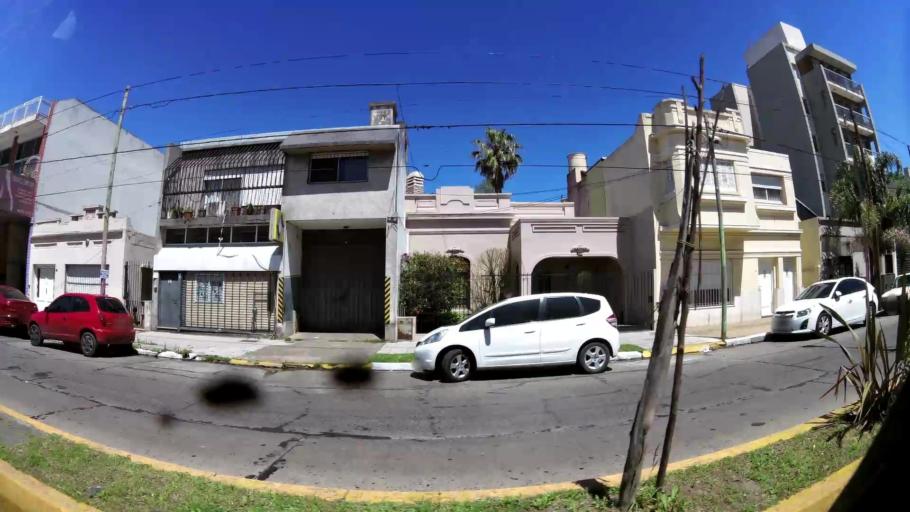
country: AR
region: Buenos Aires
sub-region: Partido de Quilmes
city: Quilmes
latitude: -34.7153
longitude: -58.2765
